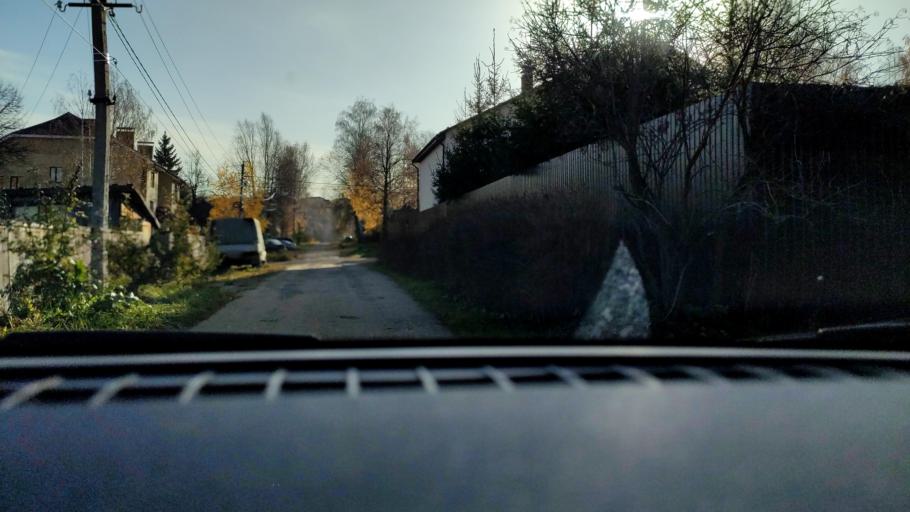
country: RU
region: Perm
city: Perm
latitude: 58.0258
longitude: 56.3157
